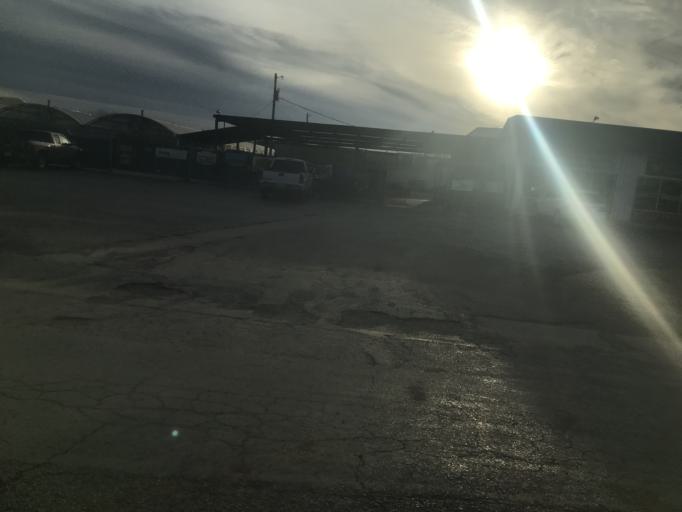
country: US
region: Texas
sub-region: Taylor County
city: Abilene
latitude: 32.4166
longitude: -99.7800
